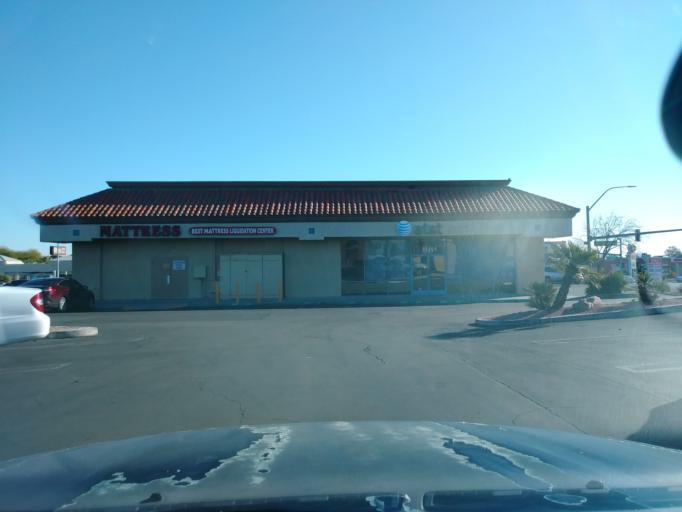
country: US
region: Nevada
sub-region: Clark County
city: Spring Valley
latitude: 36.1595
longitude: -115.2447
